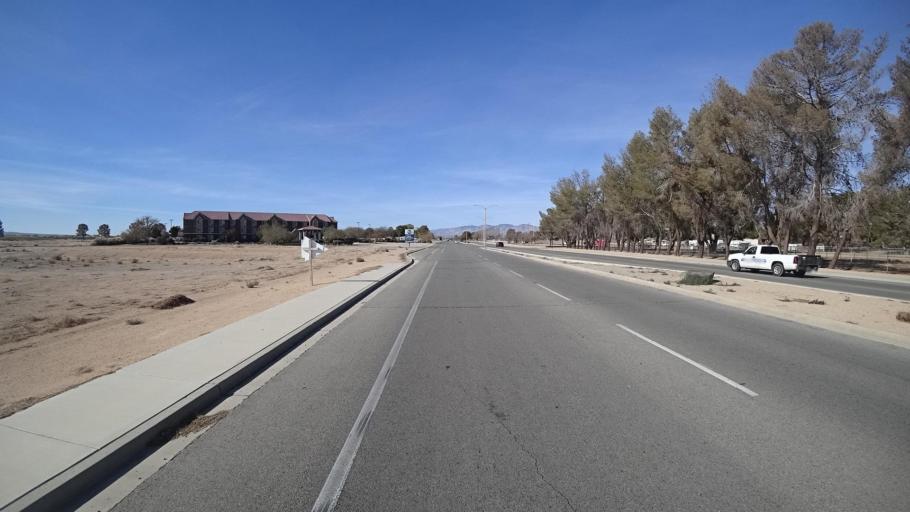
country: US
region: California
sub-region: Kern County
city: California City
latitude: 35.1259
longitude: -117.9428
